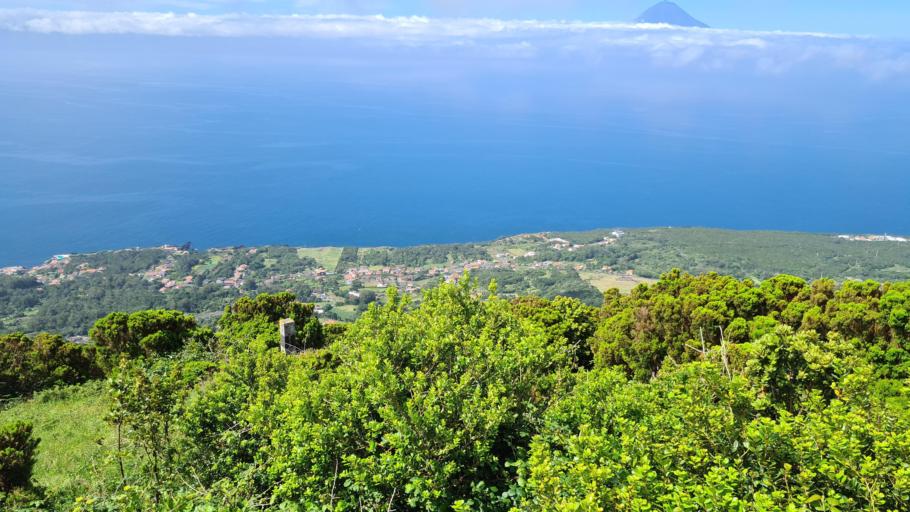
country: PT
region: Azores
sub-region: Sao Roque do Pico
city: Sao Roque do Pico
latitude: 38.6631
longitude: -28.1287
